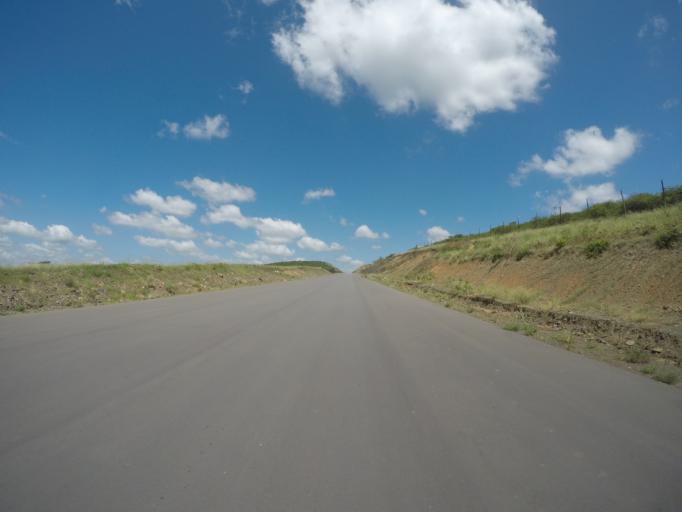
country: ZA
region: KwaZulu-Natal
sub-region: uThungulu District Municipality
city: Empangeni
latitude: -28.6211
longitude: 31.7567
